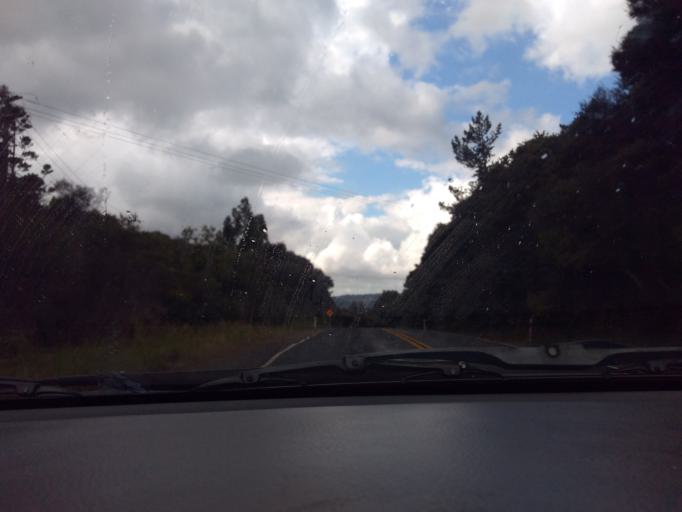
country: NZ
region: Auckland
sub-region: Auckland
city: Titirangi
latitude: -37.0020
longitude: 174.5875
